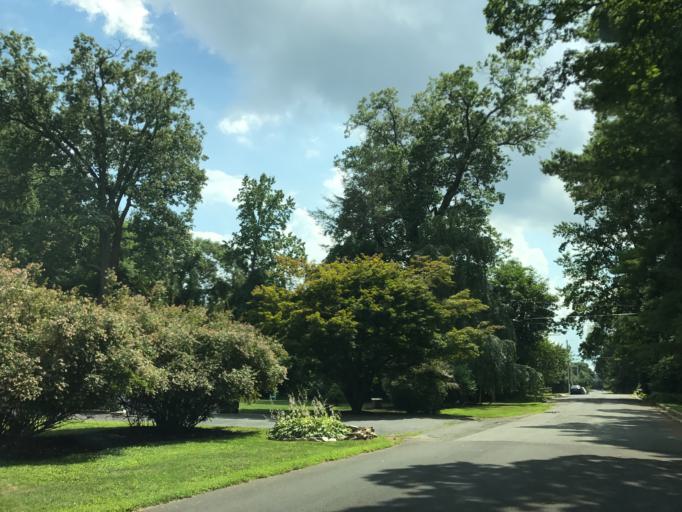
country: US
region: Maryland
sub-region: Harford County
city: North Bel Air
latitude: 39.5439
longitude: -76.3571
